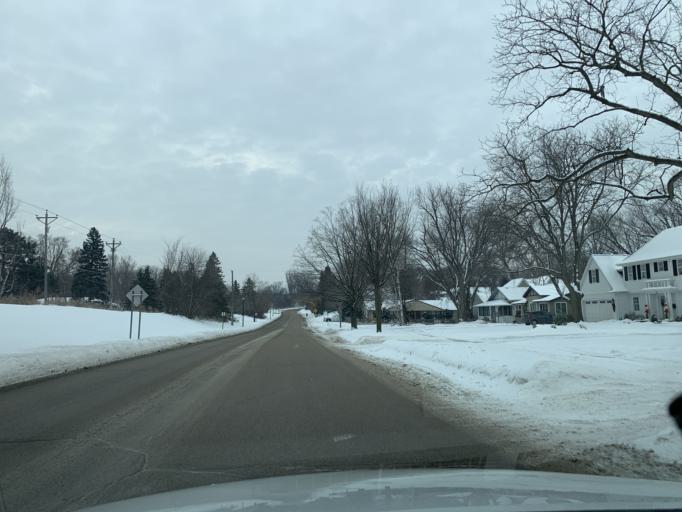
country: US
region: Minnesota
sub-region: Hennepin County
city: Edina
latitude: 44.9161
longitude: -93.3538
